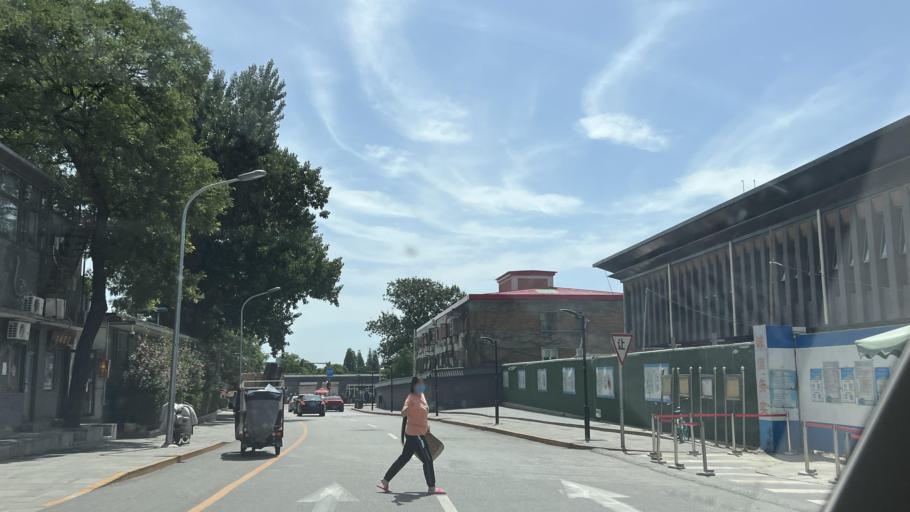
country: CN
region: Beijing
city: Xiangshan
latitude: 39.9915
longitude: 116.2026
